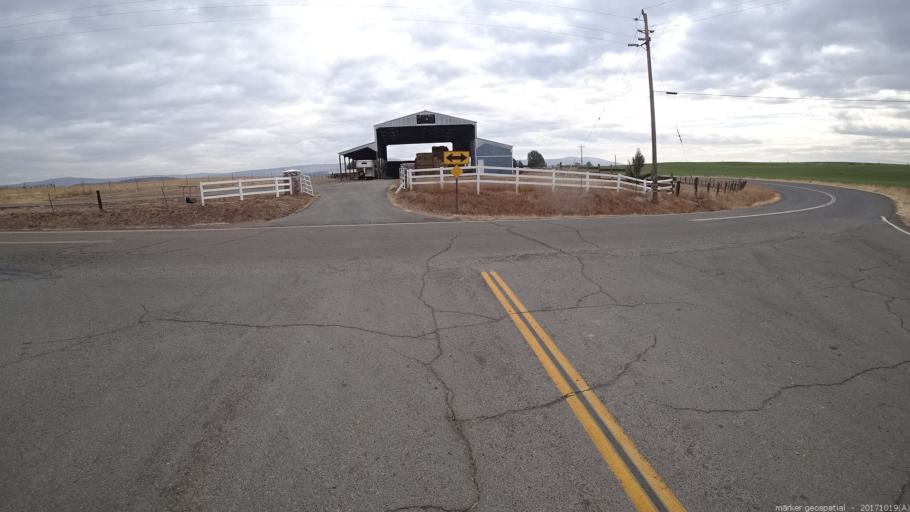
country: US
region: California
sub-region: Shasta County
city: Burney
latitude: 41.0305
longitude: -121.3315
